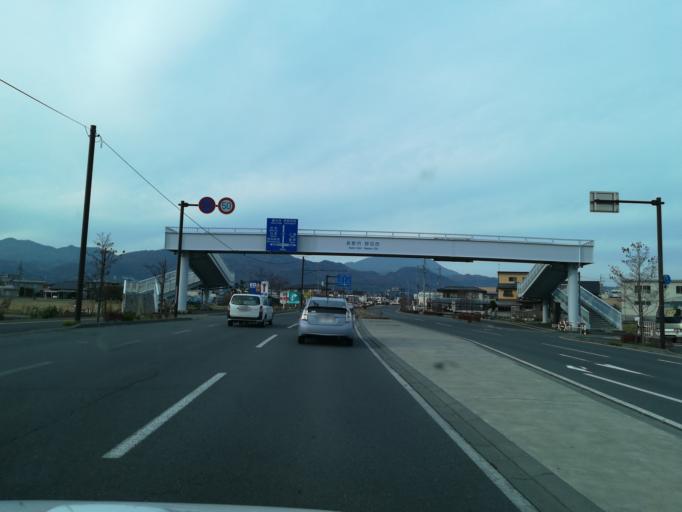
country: JP
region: Nagano
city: Nagano-shi
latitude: 36.6010
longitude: 138.1800
